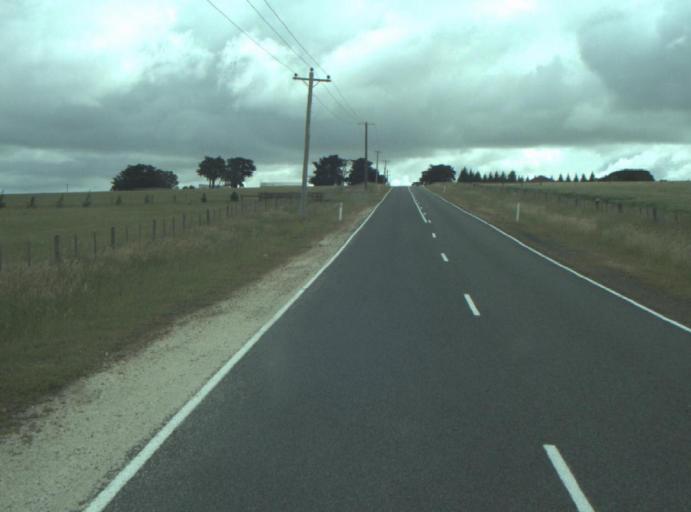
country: AU
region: Victoria
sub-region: Greater Geelong
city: Wandana Heights
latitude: -38.1768
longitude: 144.2710
